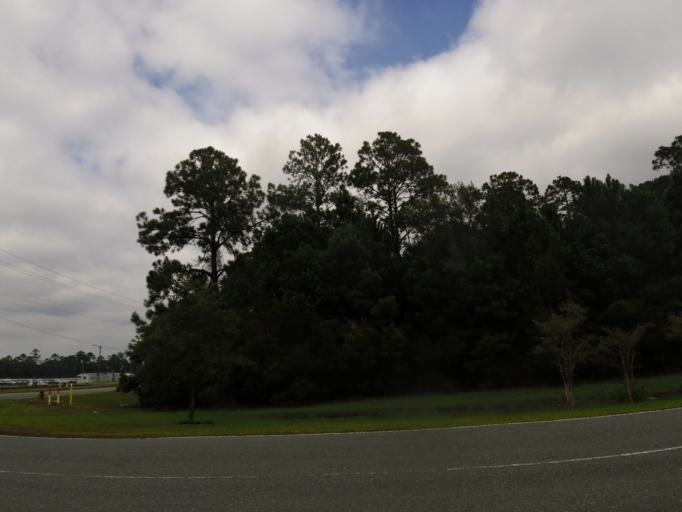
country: US
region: Georgia
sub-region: Glynn County
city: Brunswick
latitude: 31.1135
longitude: -81.5443
